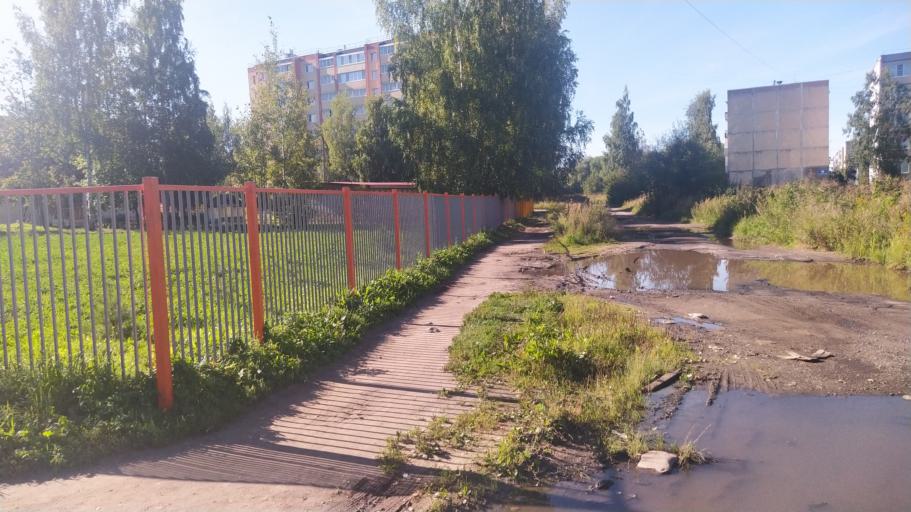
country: RU
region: Jaroslavl
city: Rybinsk
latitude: 58.0452
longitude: 38.7831
